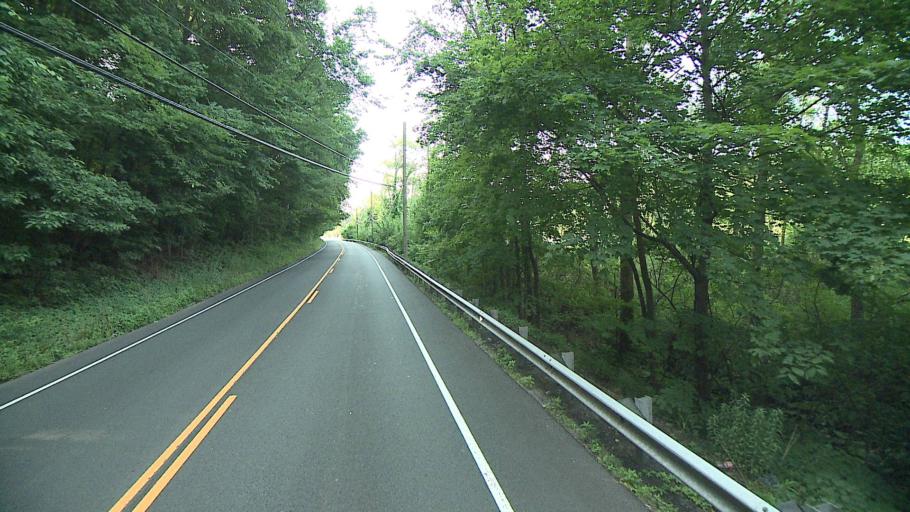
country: US
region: Connecticut
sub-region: Fairfield County
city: Ridgefield
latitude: 41.3193
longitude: -73.4753
